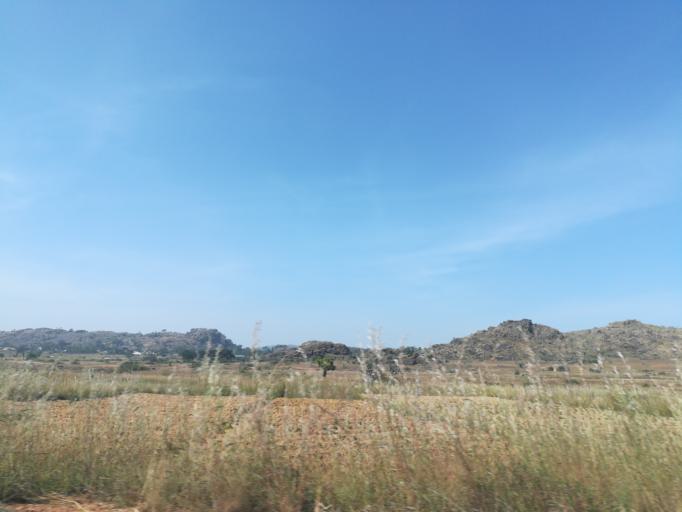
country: NG
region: Plateau
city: Bukuru
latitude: 9.7663
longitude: 8.9031
